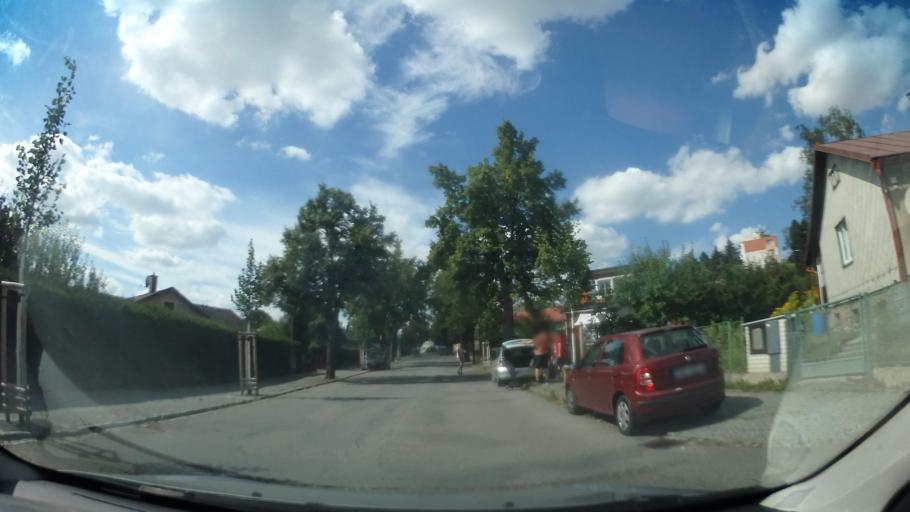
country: CZ
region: Vysocina
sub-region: Okres Zd'ar nad Sazavou
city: Zd'ar nad Sazavou
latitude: 49.5616
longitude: 15.9330
